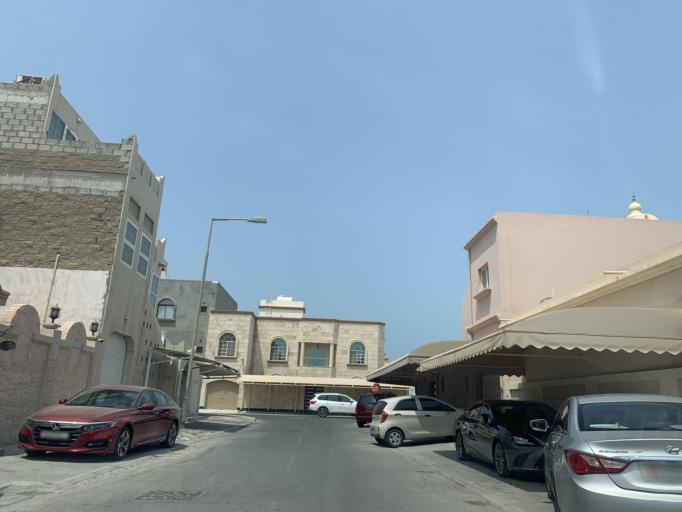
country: BH
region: Muharraq
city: Al Hadd
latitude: 26.2747
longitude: 50.6571
